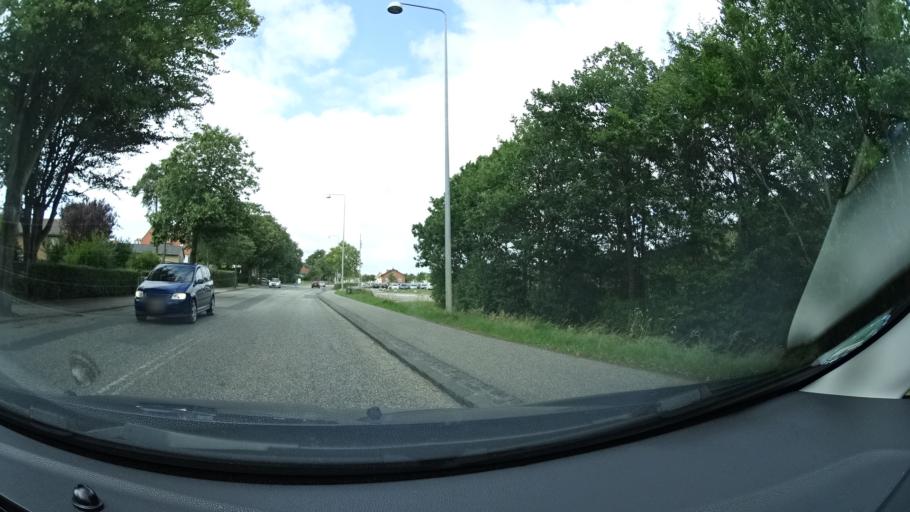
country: DK
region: Central Jutland
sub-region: Ringkobing-Skjern Kommune
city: Ringkobing
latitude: 56.0897
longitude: 8.2535
